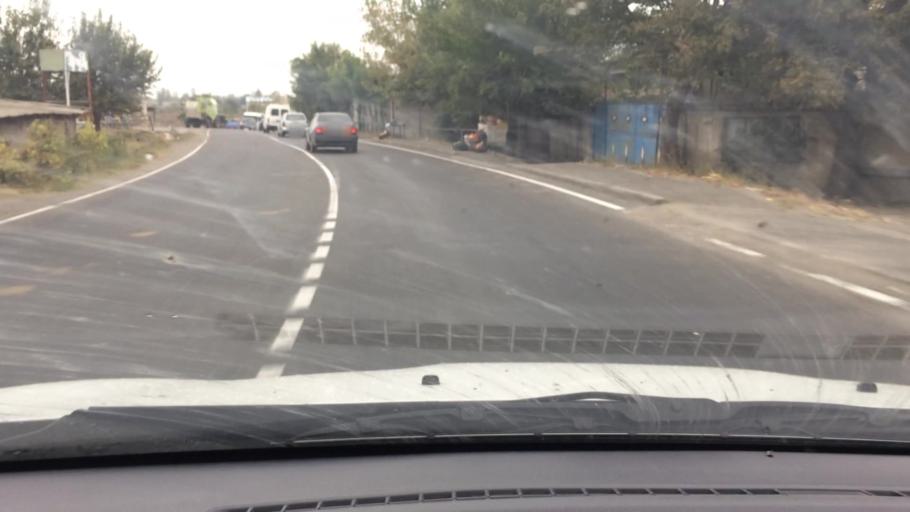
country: GE
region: Kvemo Kartli
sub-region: Marneuli
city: Marneuli
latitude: 41.4017
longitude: 44.8279
